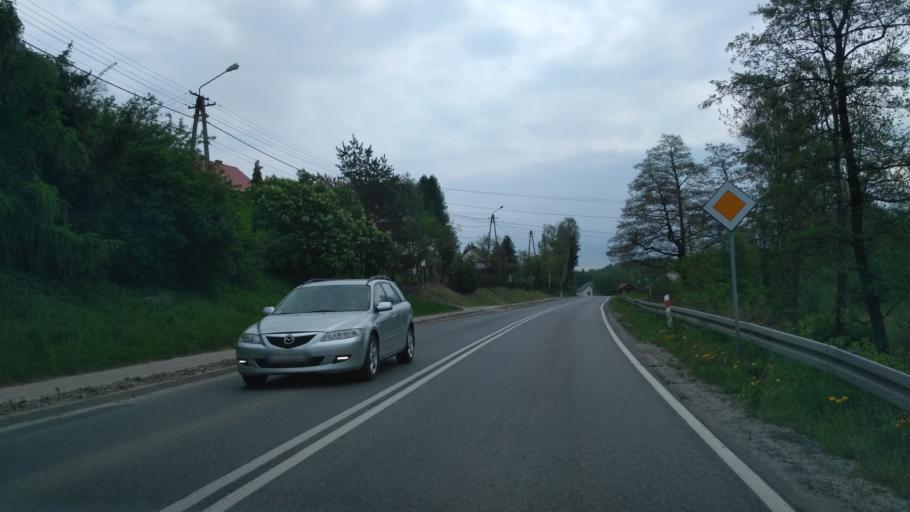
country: PL
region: Lesser Poland Voivodeship
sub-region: Powiat tarnowski
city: Tarnowiec
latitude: 49.9573
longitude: 20.9987
